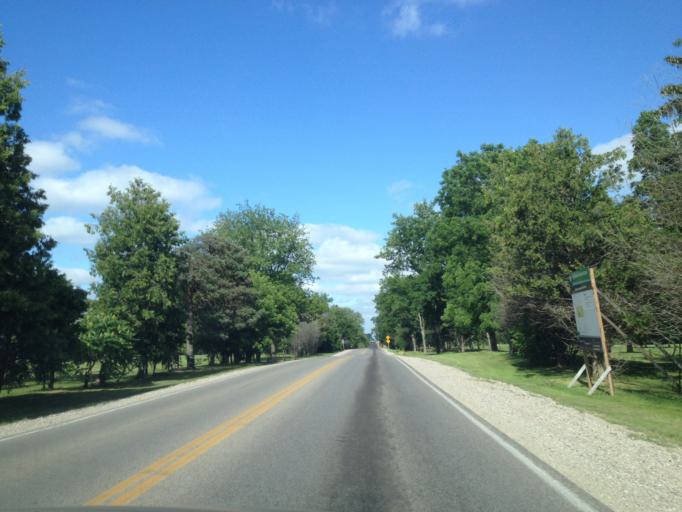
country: CA
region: Ontario
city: London
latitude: 43.0322
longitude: -81.3097
